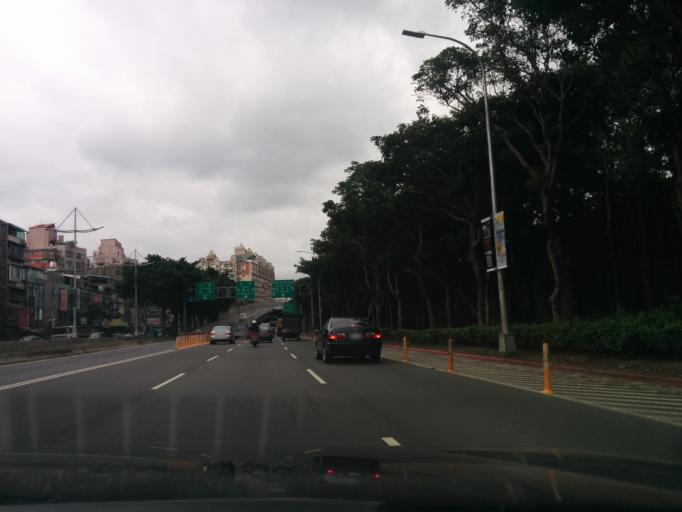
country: TW
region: Taipei
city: Taipei
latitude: 25.0880
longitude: 121.5037
